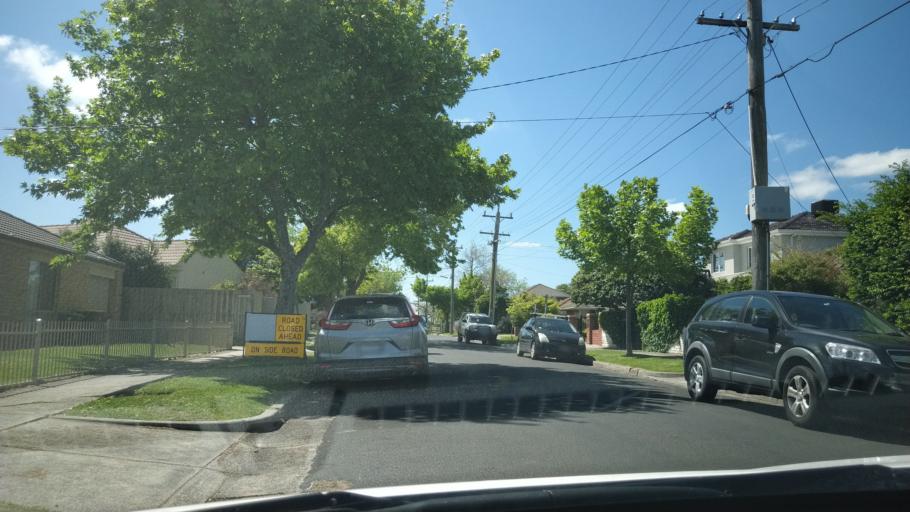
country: AU
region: Victoria
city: Murrumbeena
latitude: -37.9064
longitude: 145.0688
